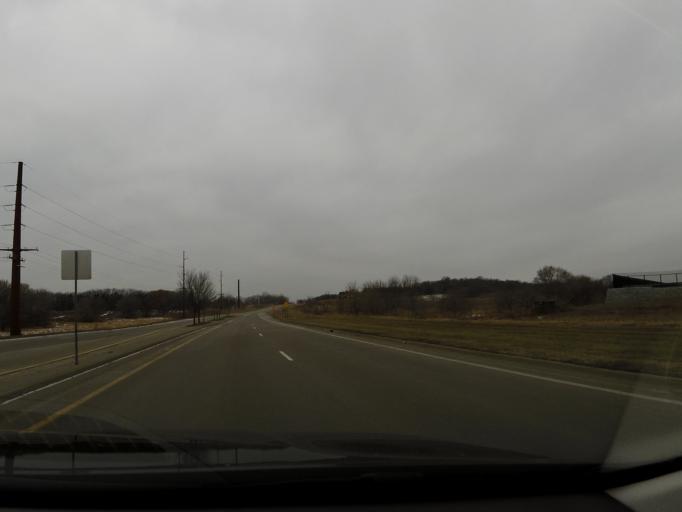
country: US
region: Minnesota
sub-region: Carver County
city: Chaska
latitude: 44.8058
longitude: -93.6359
